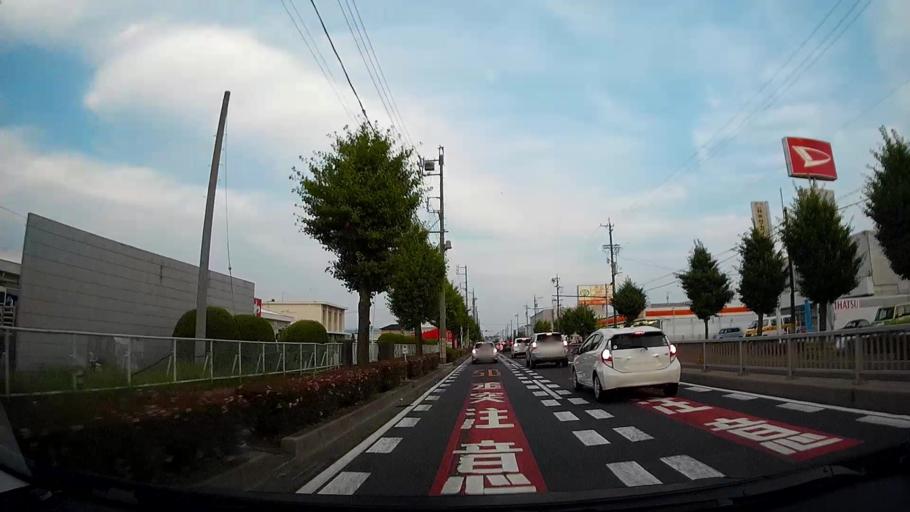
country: JP
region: Aichi
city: Toyohashi
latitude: 34.7846
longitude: 137.3791
